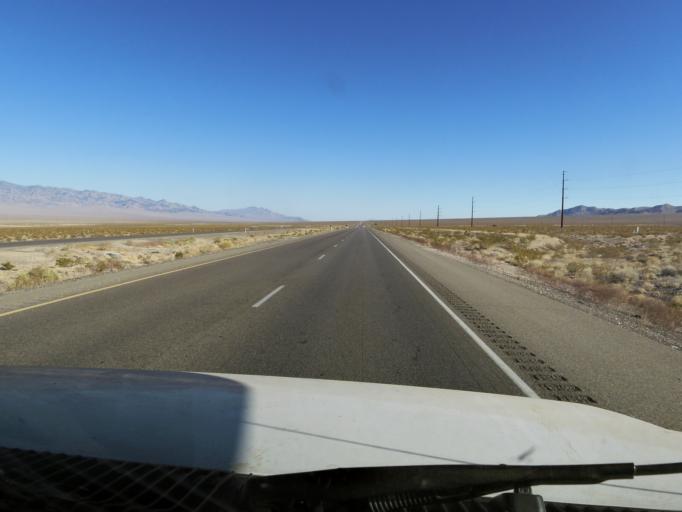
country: US
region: Nevada
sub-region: Clark County
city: Summerlin South
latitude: 36.5271
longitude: -115.5545
